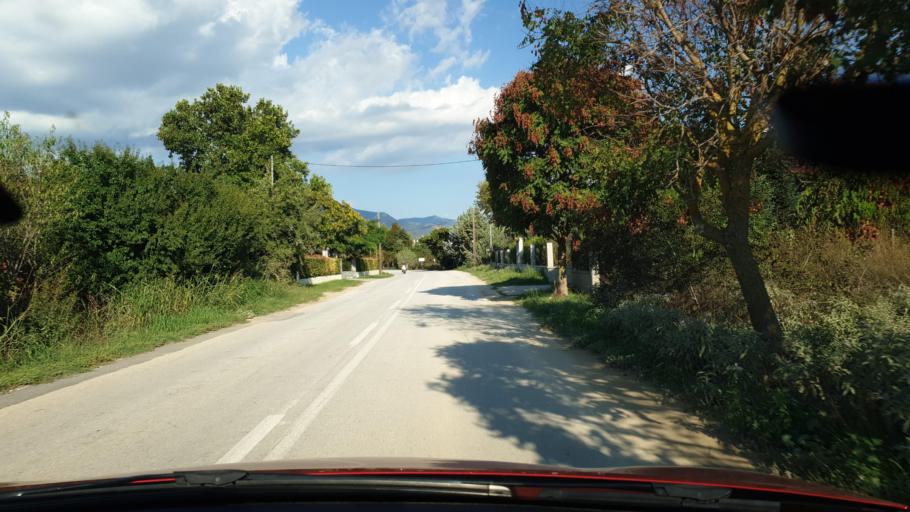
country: GR
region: Central Macedonia
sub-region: Nomos Thessalonikis
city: Souroti
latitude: 40.4762
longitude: 23.1066
